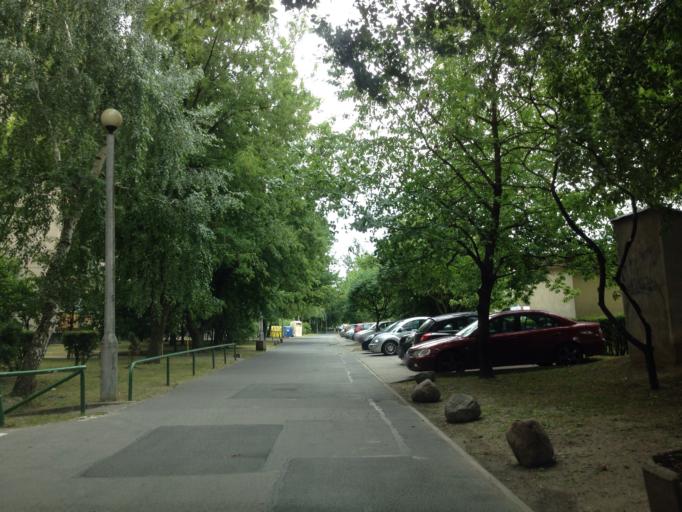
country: PL
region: Masovian Voivodeship
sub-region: Warszawa
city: Bemowo
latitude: 52.2559
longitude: 20.9250
